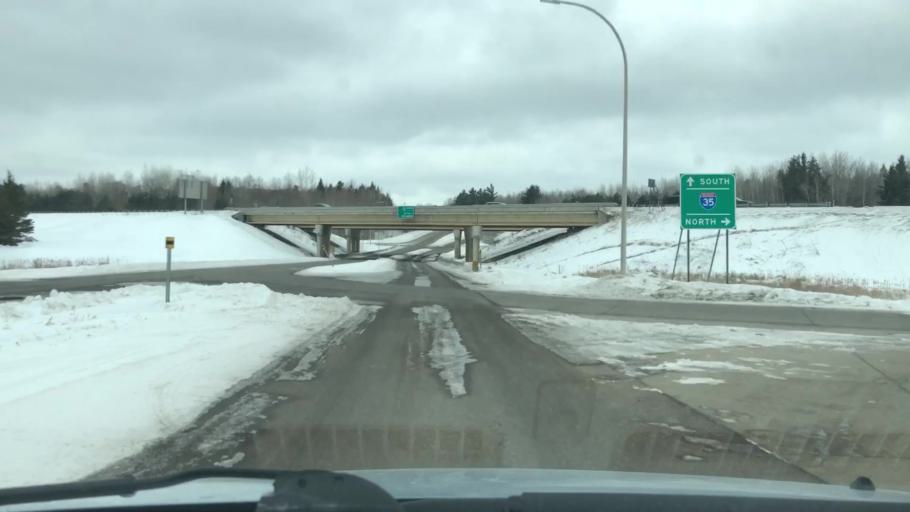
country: US
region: Minnesota
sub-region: Carlton County
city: Esko
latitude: 46.7025
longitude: -92.3001
